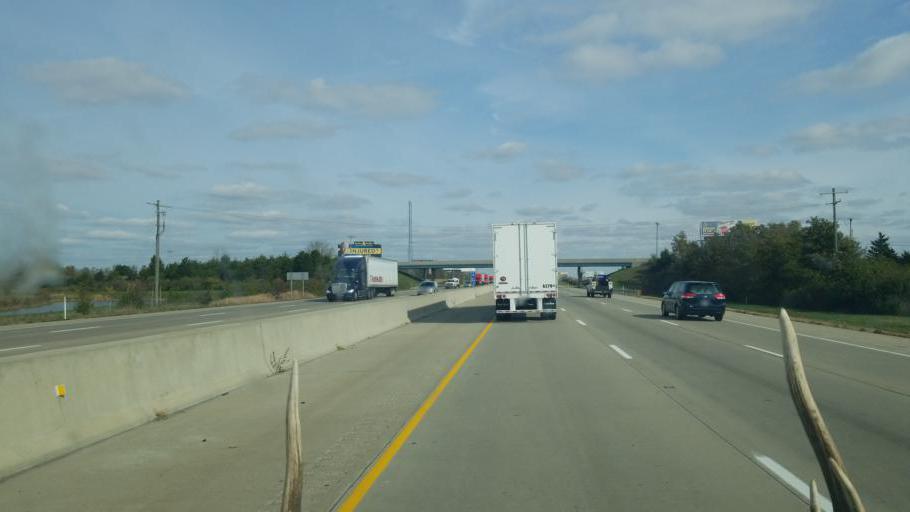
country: US
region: Indiana
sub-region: Marion County
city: Cumberland
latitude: 39.8123
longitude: -85.9361
